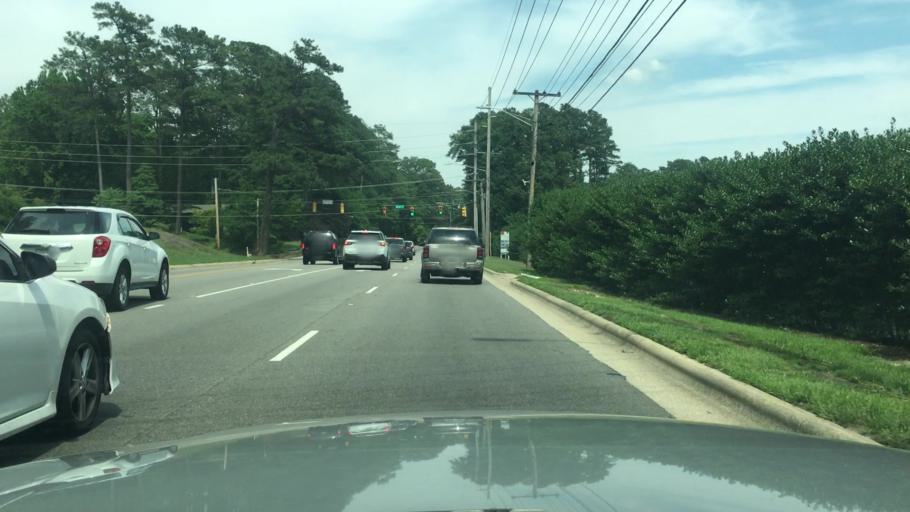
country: US
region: North Carolina
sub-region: Cumberland County
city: Fayetteville
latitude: 35.0639
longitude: -78.9279
